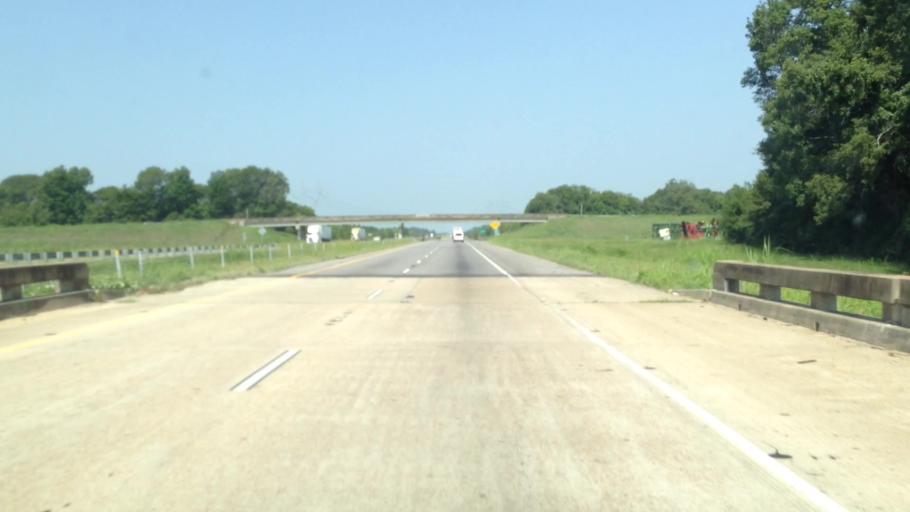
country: US
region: Louisiana
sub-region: Madison Parish
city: Tallulah
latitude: 32.4193
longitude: -91.2983
